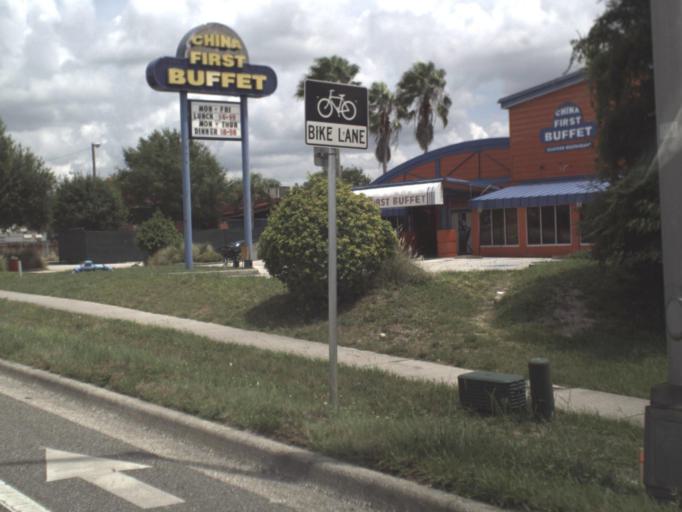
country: US
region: Florida
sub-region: Hillsborough County
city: University
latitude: 28.0543
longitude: -82.4285
